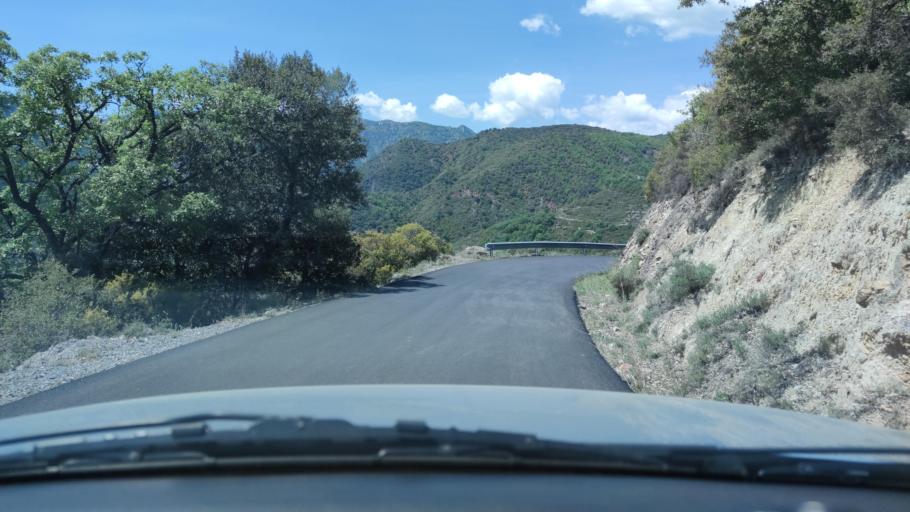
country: ES
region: Catalonia
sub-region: Provincia de Lleida
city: Sort
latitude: 42.3104
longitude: 1.0674
